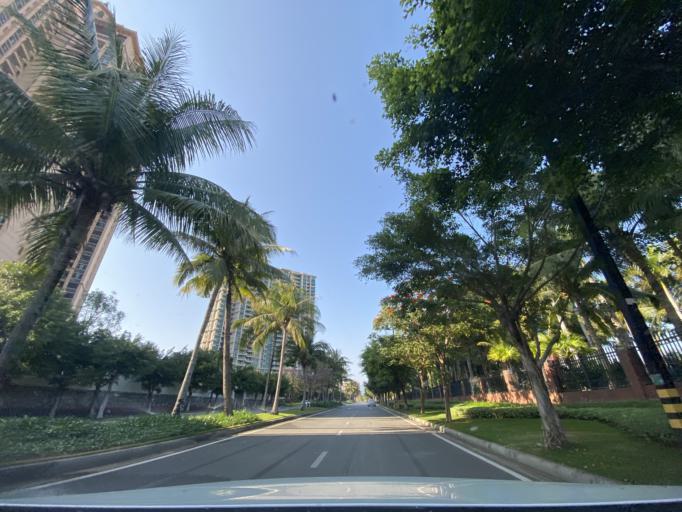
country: CN
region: Hainan
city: Yingzhou
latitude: 18.4124
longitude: 109.8900
